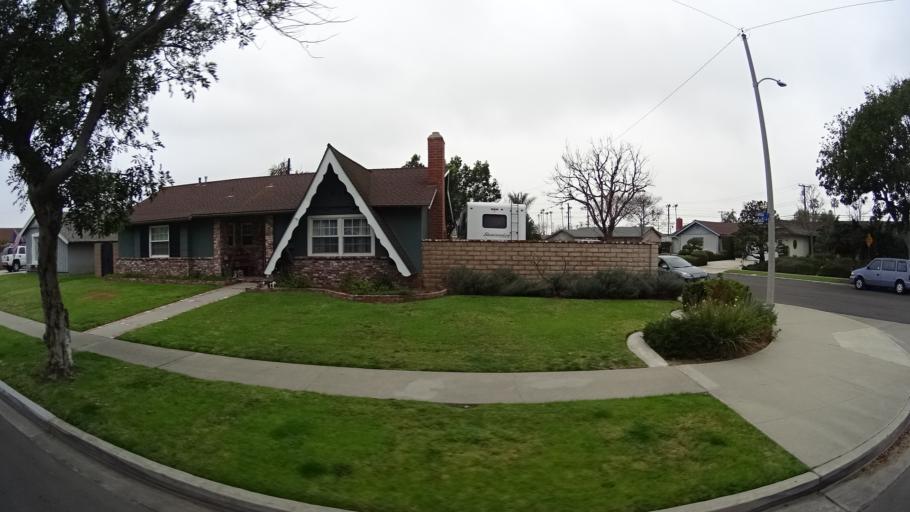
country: US
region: California
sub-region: Orange County
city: Stanton
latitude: 33.8213
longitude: -118.0091
